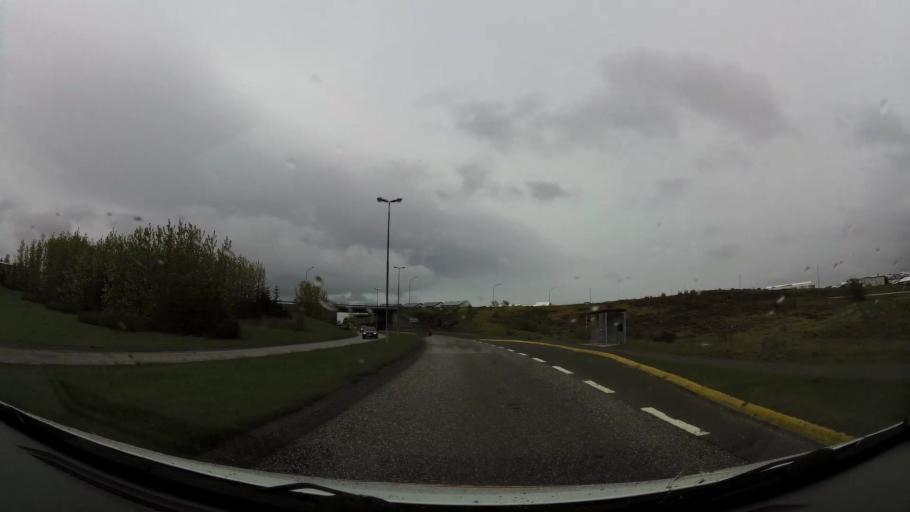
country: IS
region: Capital Region
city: Hafnarfjoerdur
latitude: 64.0548
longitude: -21.9664
